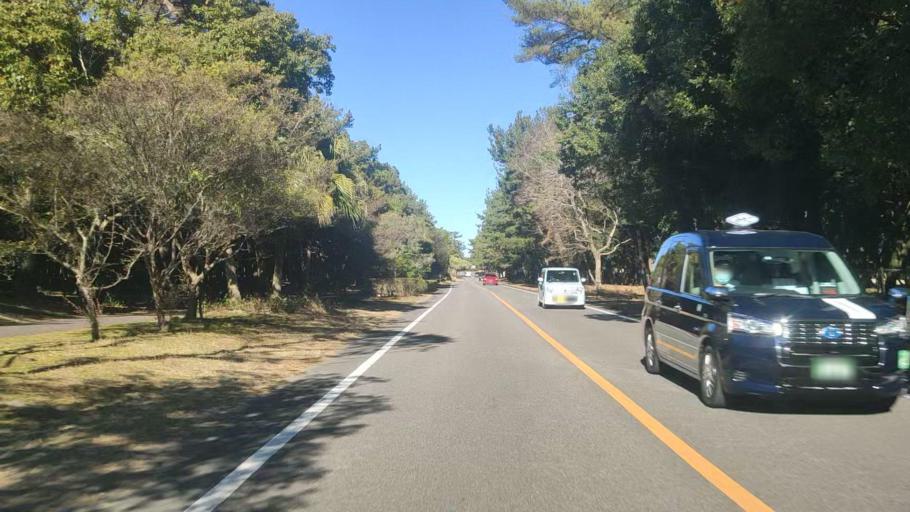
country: JP
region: Miyazaki
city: Miyazaki-shi
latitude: 31.9490
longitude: 131.4658
